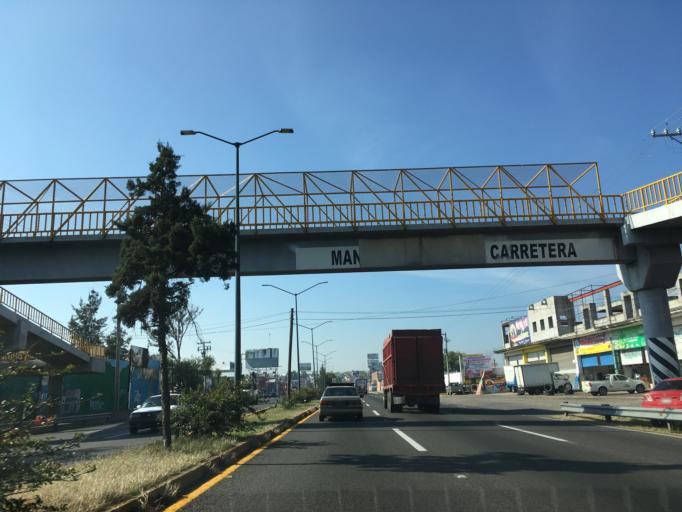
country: MX
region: Michoacan
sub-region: Tarimbaro
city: Fraccionamiento Privadas del Sol
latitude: 19.7449
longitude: -101.1748
